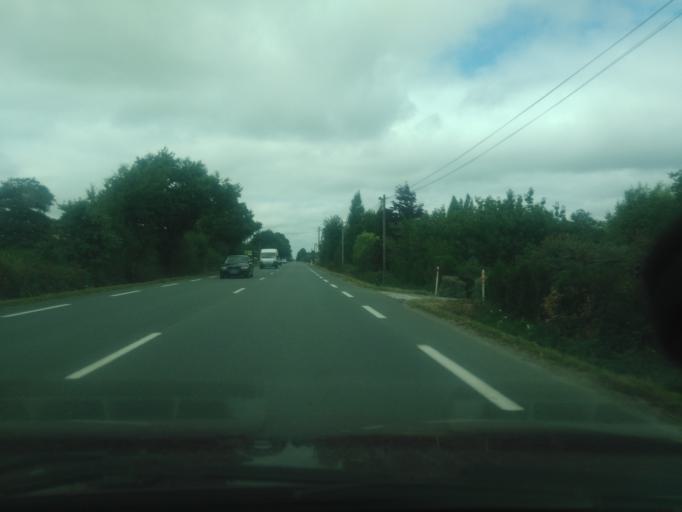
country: FR
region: Pays de la Loire
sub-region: Departement de la Vendee
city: La Ferriere
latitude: 46.7011
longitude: -1.3437
